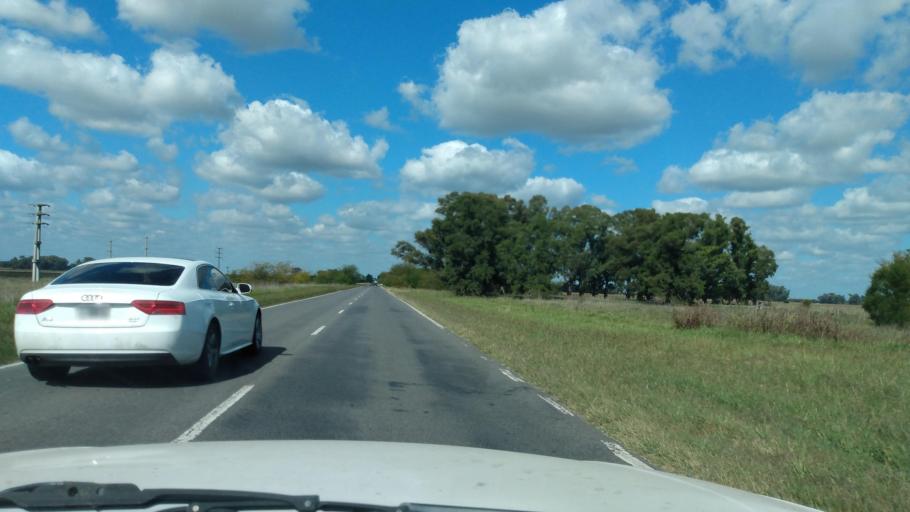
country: AR
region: Buenos Aires
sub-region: Partido de Navarro
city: Navarro
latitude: -34.9212
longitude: -59.3275
